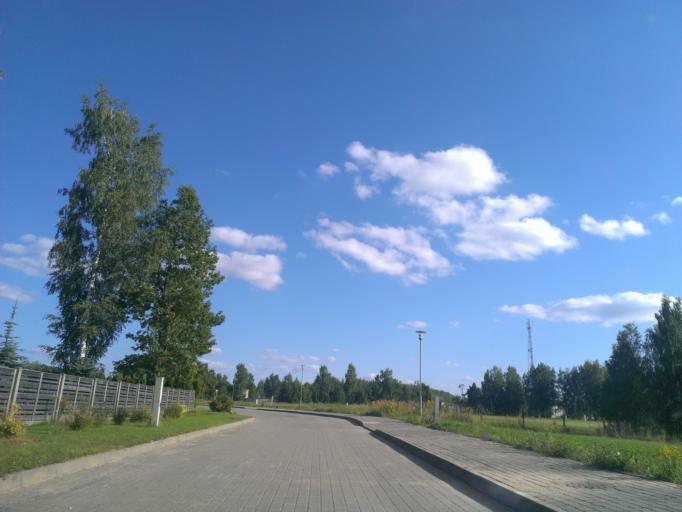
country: LV
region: Sigulda
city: Sigulda
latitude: 57.1673
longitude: 24.8764
